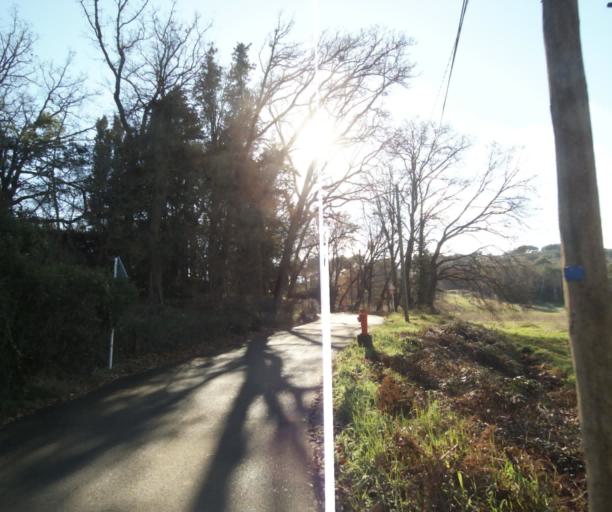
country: FR
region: Provence-Alpes-Cote d'Azur
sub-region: Departement des Alpes-Maritimes
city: Biot
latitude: 43.6152
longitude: 7.1036
